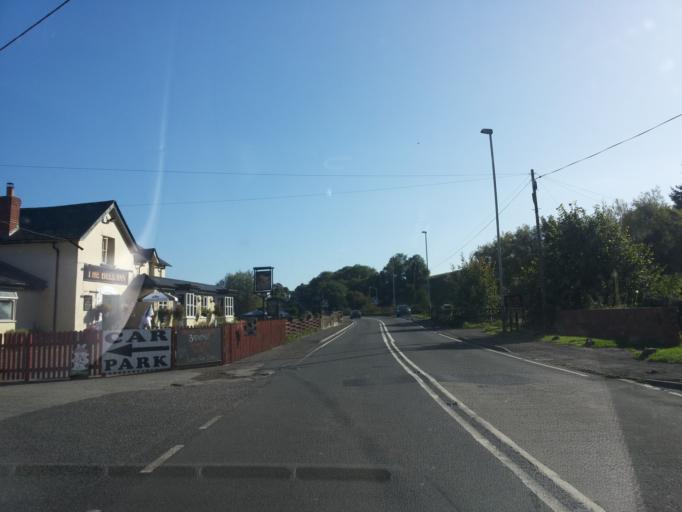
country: GB
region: England
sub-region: Wiltshire
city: Winterbourne Stoke
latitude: 51.1689
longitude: -1.8917
